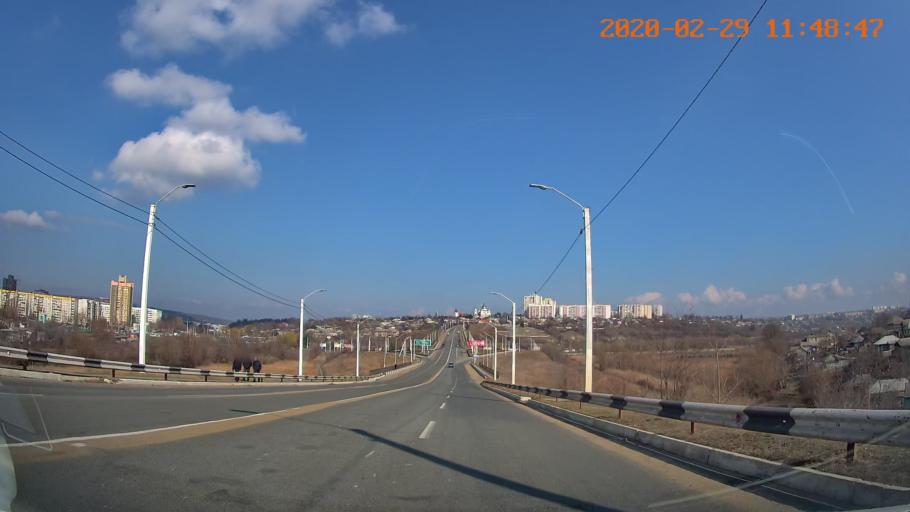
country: MD
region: Telenesti
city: Ribnita
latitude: 47.7502
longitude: 28.9923
